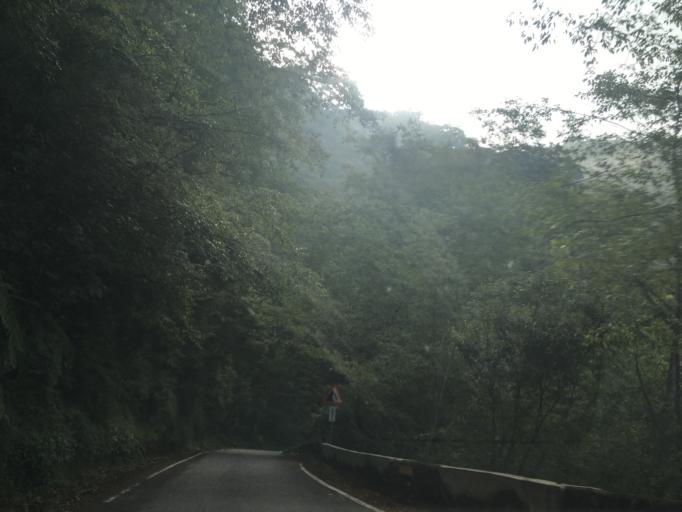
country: TW
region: Taiwan
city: Fengyuan
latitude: 24.2364
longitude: 120.9775
